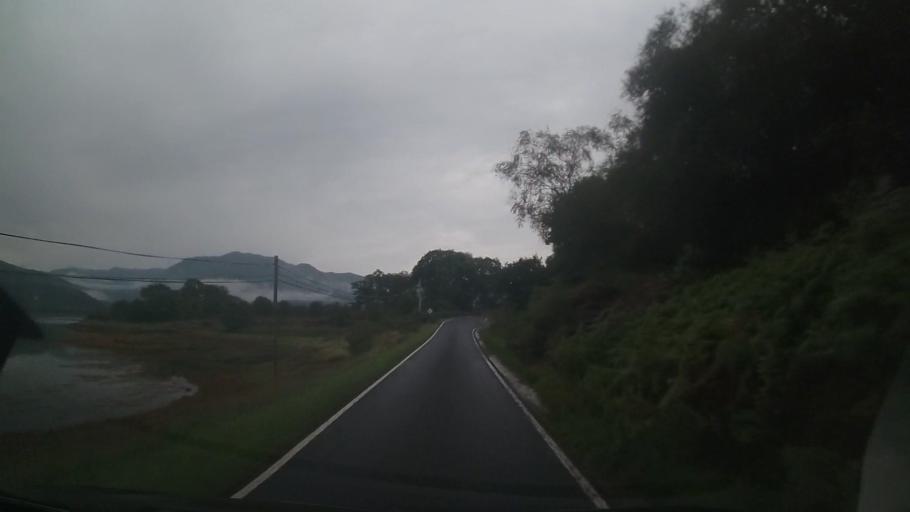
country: GB
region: Scotland
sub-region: Argyll and Bute
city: Isle Of Mull
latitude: 56.6892
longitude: -5.6654
